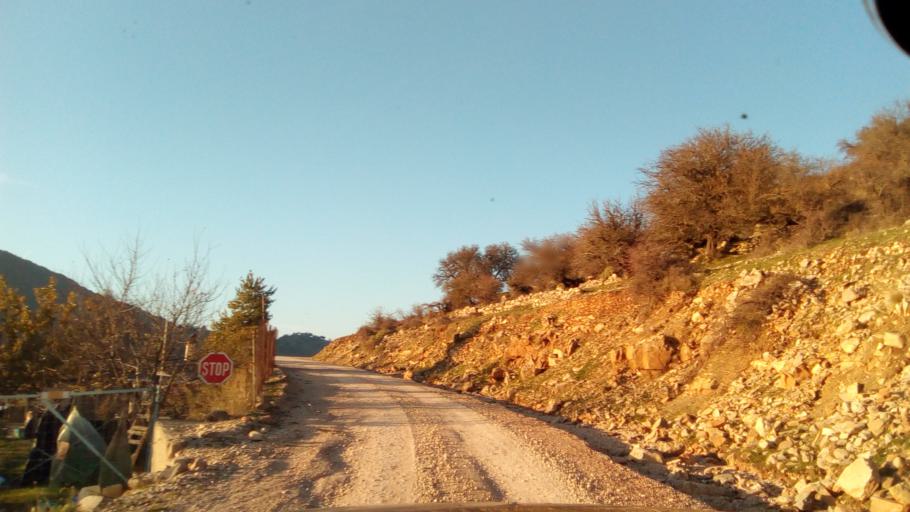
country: GR
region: West Greece
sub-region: Nomos Aitolias kai Akarnanias
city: Nafpaktos
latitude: 38.4511
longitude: 21.8444
